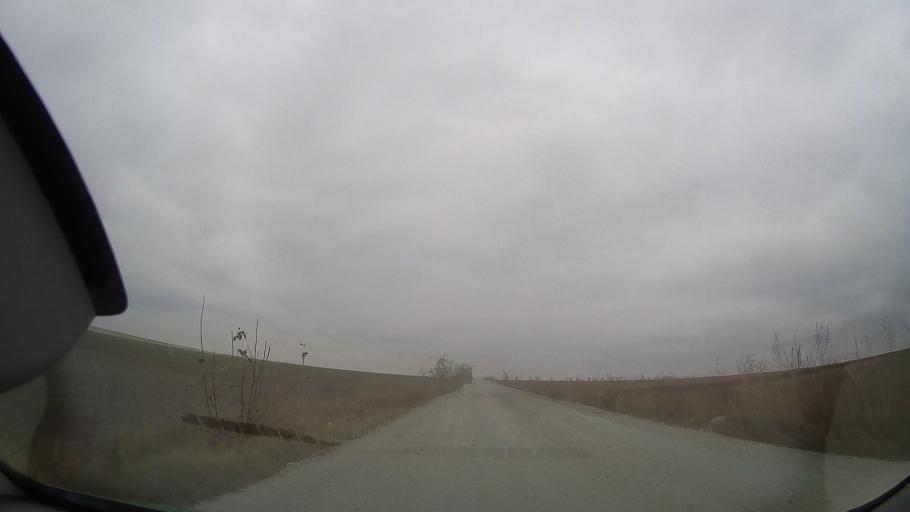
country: RO
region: Ialomita
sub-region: Comuna Grivita
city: Grivita
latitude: 44.7496
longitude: 27.2657
